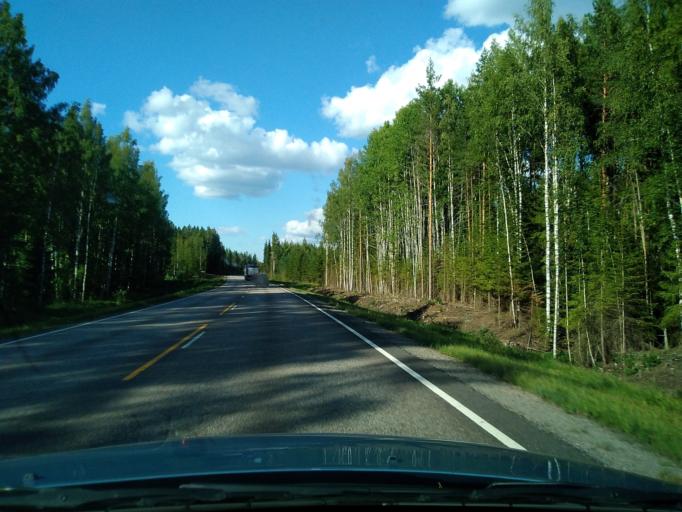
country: FI
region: Pirkanmaa
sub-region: Ylae-Pirkanmaa
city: Maenttae
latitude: 62.1064
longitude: 24.7384
